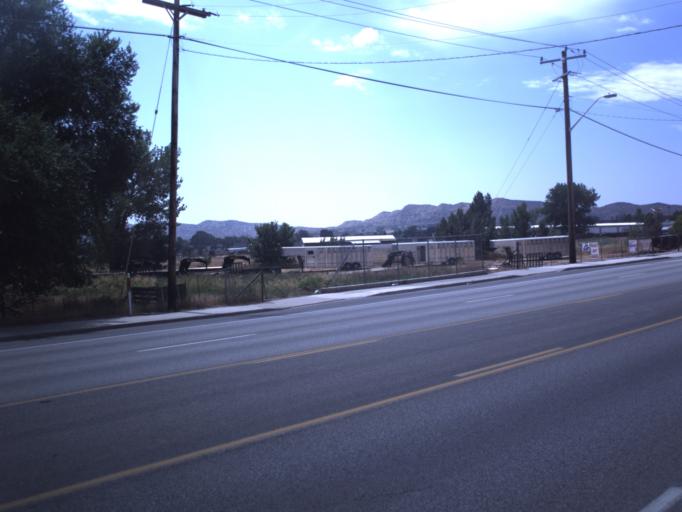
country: US
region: Utah
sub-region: Uintah County
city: Vernal
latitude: 40.4436
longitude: -109.5595
